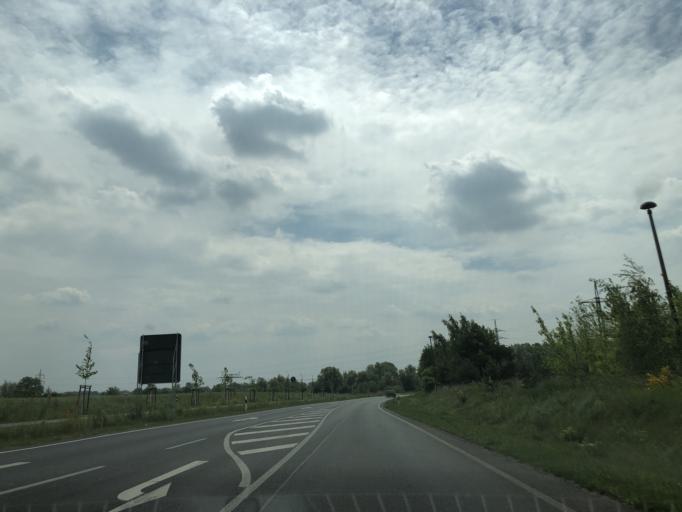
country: DE
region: Brandenburg
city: Kyritz
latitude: 52.9503
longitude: 12.4028
